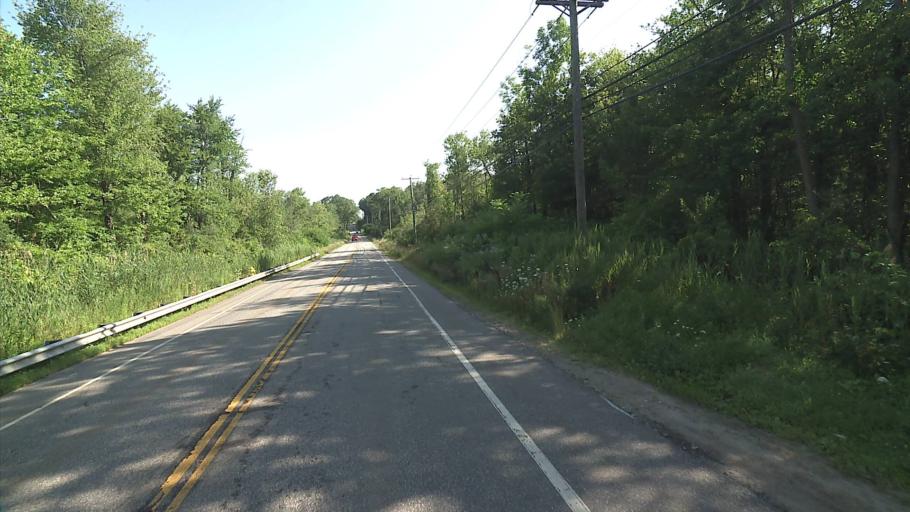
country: US
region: Connecticut
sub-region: Litchfield County
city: Torrington
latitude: 41.8409
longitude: -73.0756
